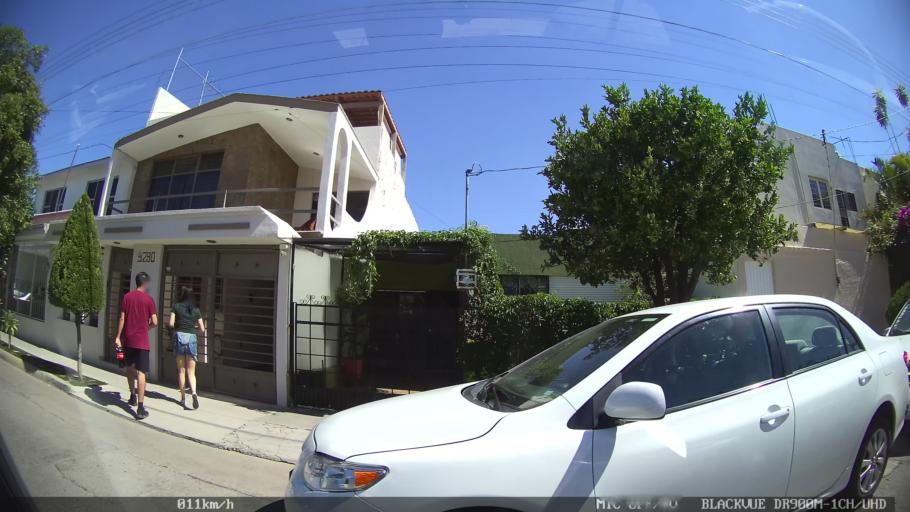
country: MX
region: Jalisco
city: Tlaquepaque
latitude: 20.6469
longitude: -103.2931
